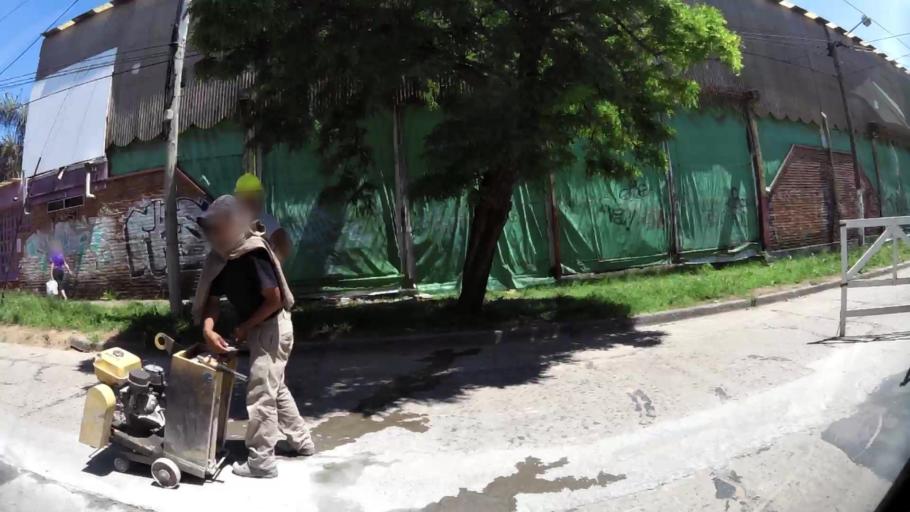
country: AR
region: Buenos Aires
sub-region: Partido de Merlo
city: Merlo
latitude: -34.6671
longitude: -58.6896
